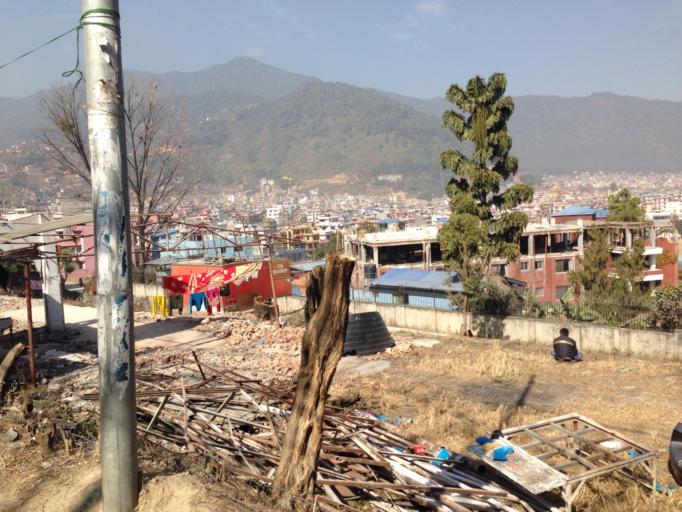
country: NP
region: Central Region
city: Kirtipur
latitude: 27.7177
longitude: 85.2820
